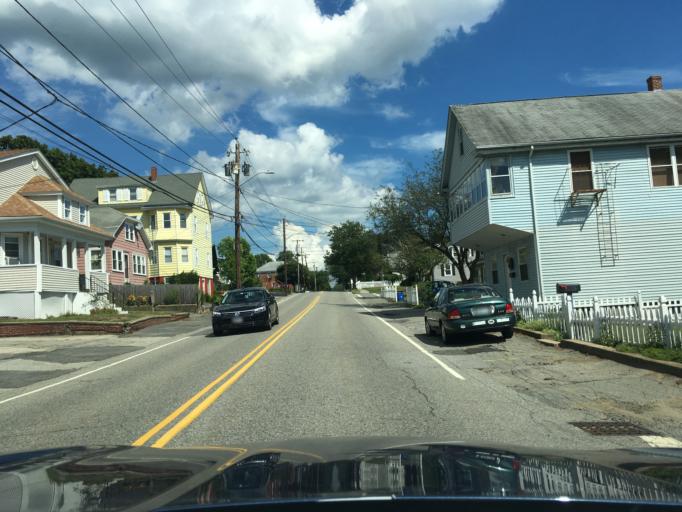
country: US
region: Rhode Island
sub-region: Bristol County
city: Barrington
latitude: 41.7389
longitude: -71.3208
